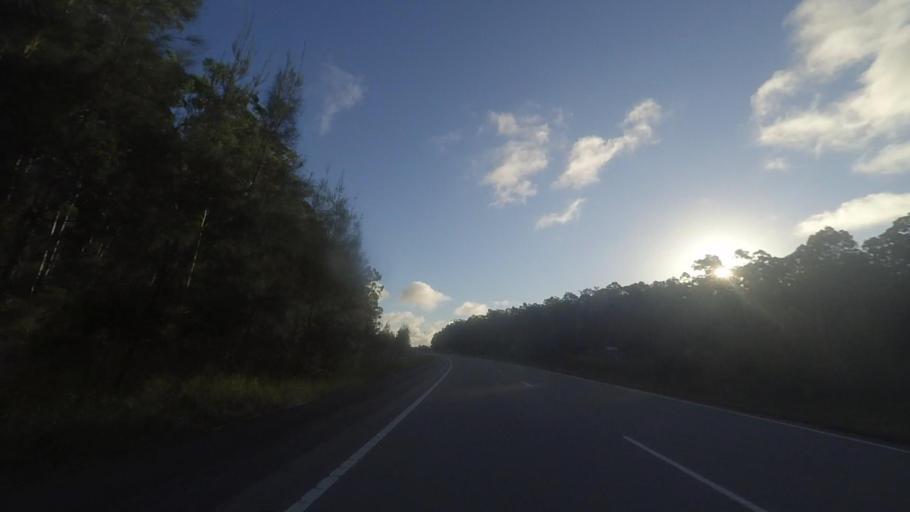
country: AU
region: New South Wales
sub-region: Great Lakes
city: Hawks Nest
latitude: -32.5502
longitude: 152.1526
